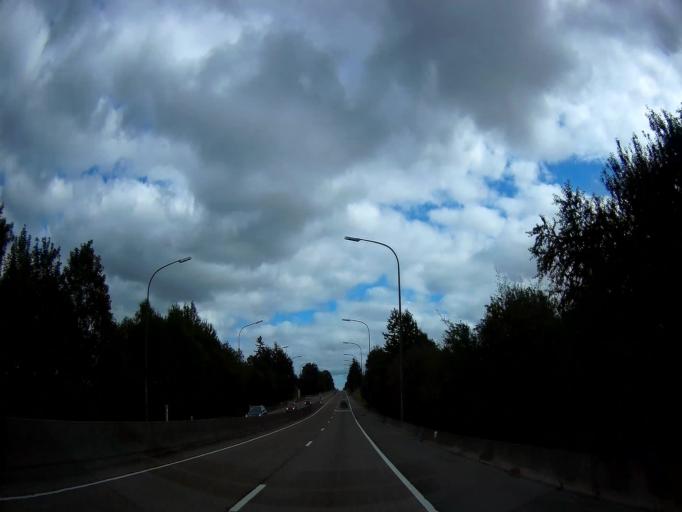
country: BE
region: Wallonia
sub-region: Province du Luxembourg
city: Sainte-Ode
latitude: 50.0409
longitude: 5.5758
